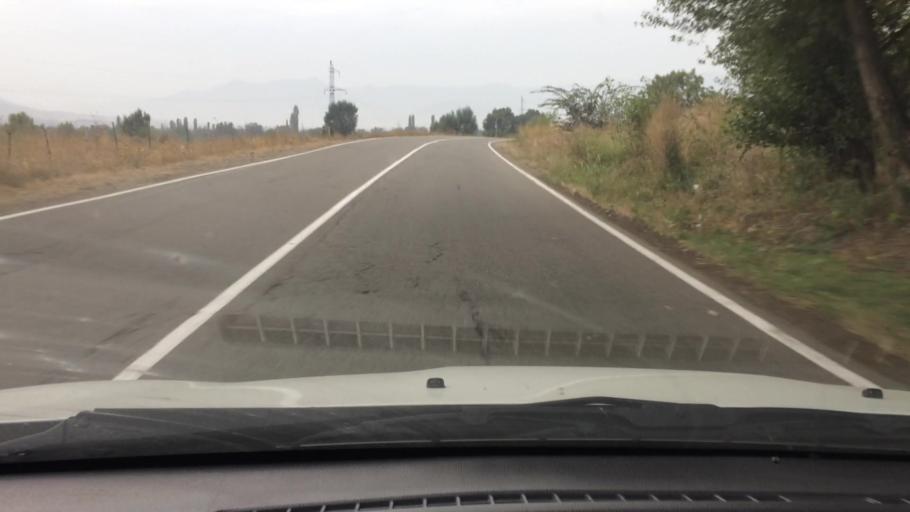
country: GE
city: Naghvarevi
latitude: 41.3151
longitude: 44.7933
